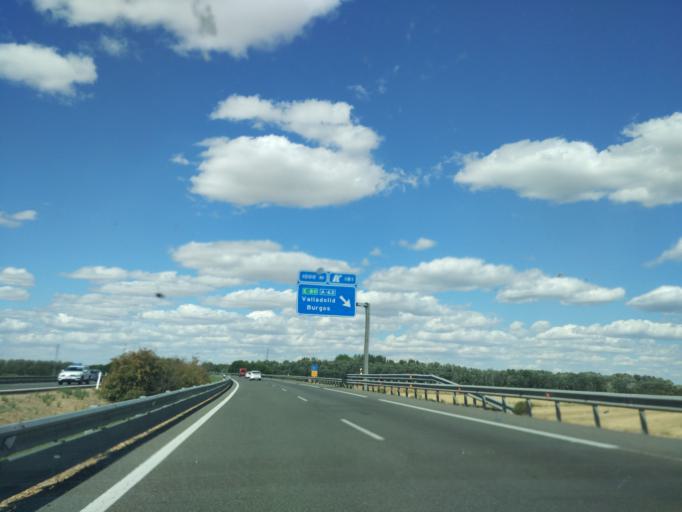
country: ES
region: Castille and Leon
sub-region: Provincia de Valladolid
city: Tordesillas
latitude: 41.4844
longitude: -4.9875
